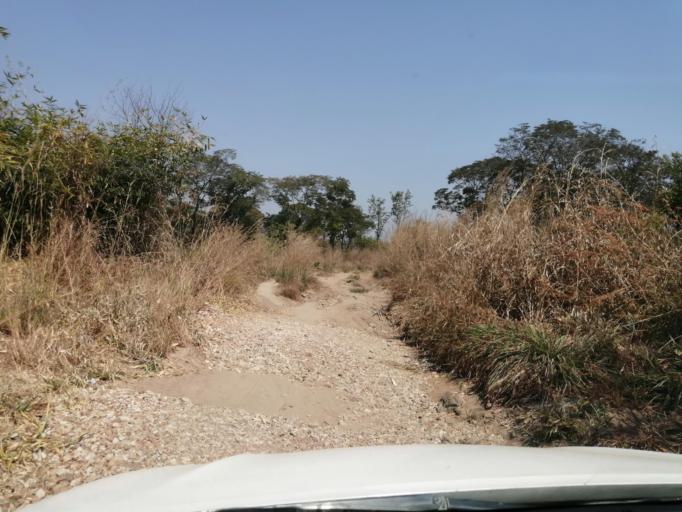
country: ZM
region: Eastern
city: Nyimba
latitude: -14.3104
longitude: 30.0514
